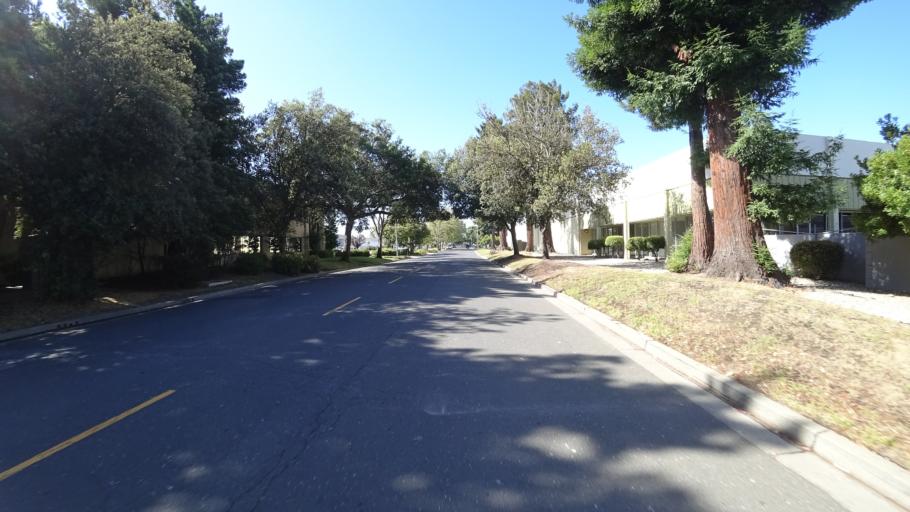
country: US
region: California
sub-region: Alameda County
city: Union City
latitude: 37.6141
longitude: -122.0484
